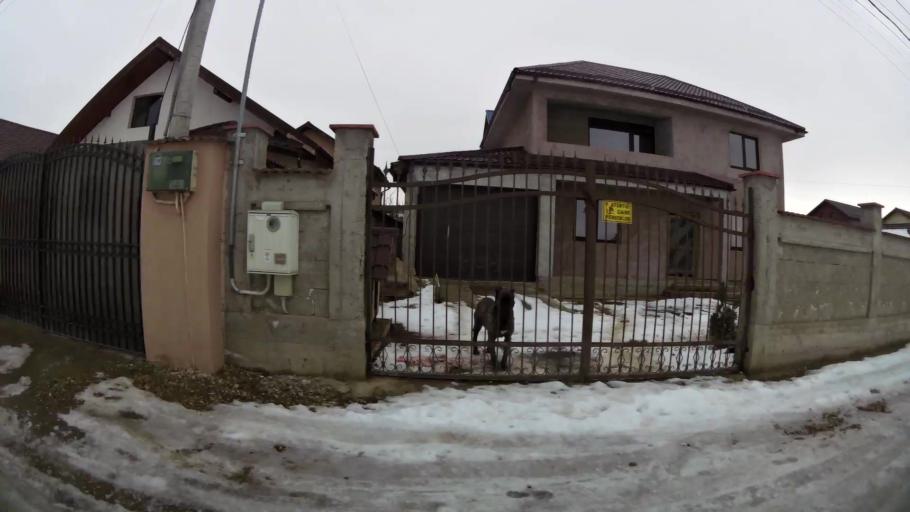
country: RO
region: Ilfov
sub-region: Comuna Pantelimon
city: Pantelimon
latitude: 44.4662
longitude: 26.2048
